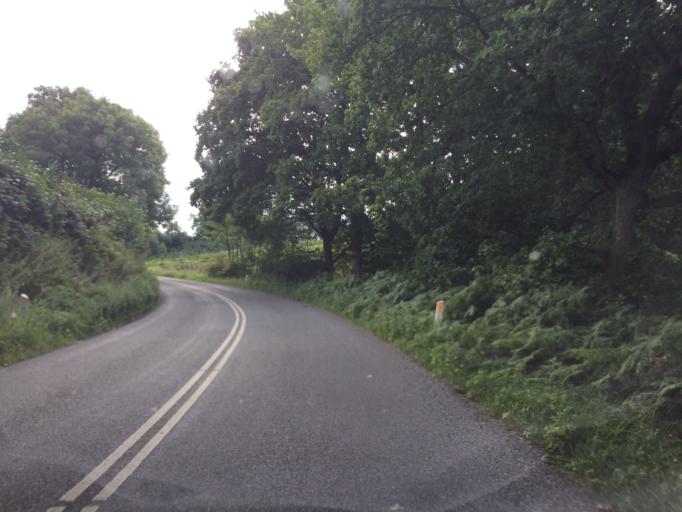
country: DK
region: South Denmark
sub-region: Faaborg-Midtfyn Kommune
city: Faaborg
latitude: 55.1531
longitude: 10.2635
